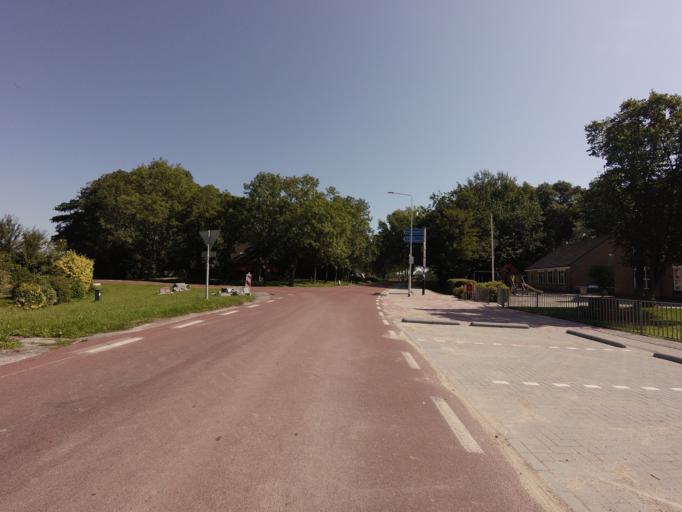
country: NL
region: Friesland
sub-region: Gemeente Dongeradeel
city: Ternaard
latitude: 53.3630
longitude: 5.9806
